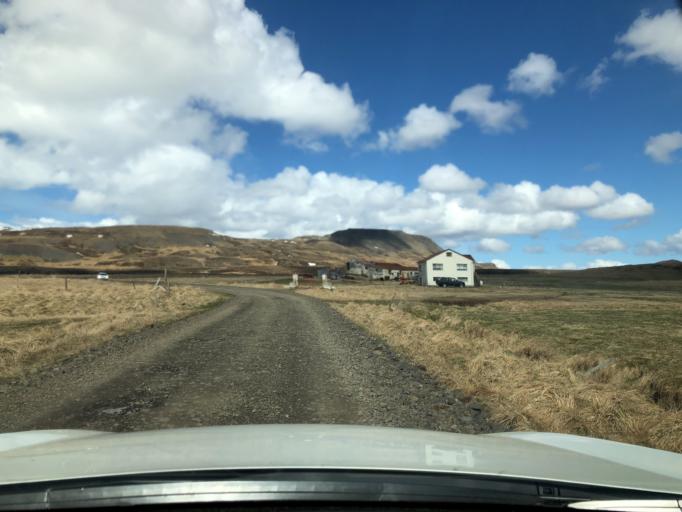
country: IS
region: West
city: Stykkisholmur
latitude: 64.8525
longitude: -22.3719
